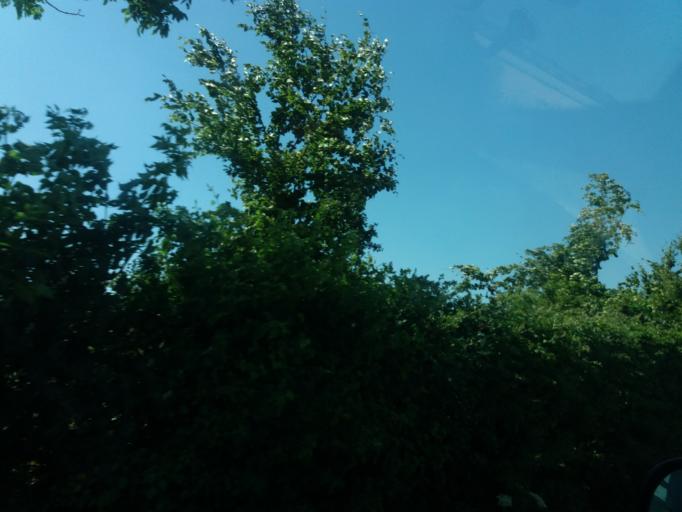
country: IE
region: Leinster
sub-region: An Mhi
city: Ashbourne
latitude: 53.5454
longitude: -6.3248
